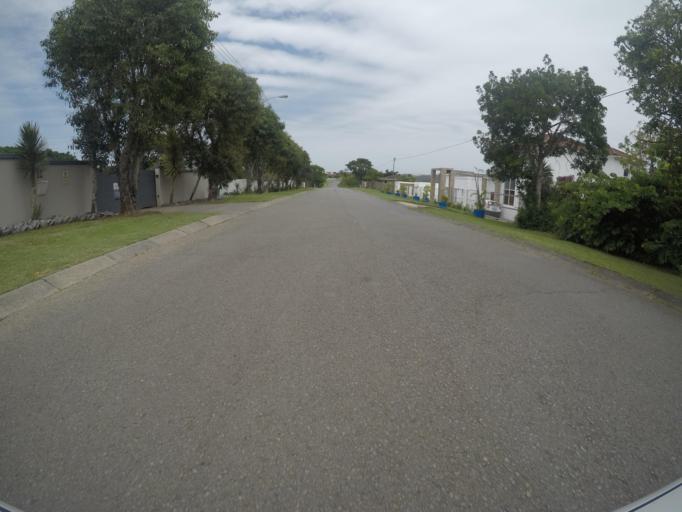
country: ZA
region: Eastern Cape
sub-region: Buffalo City Metropolitan Municipality
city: East London
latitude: -32.9627
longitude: 27.9286
